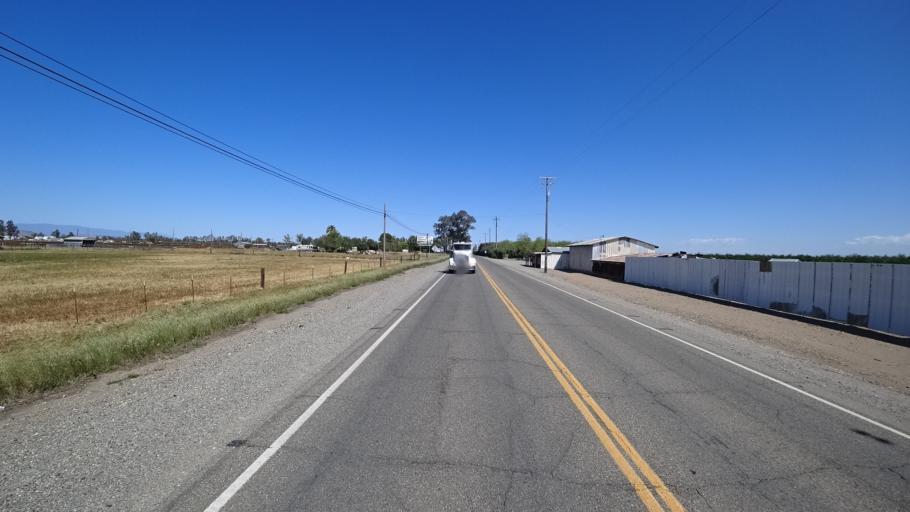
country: US
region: California
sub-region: Glenn County
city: Orland
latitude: 39.6980
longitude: -122.1965
